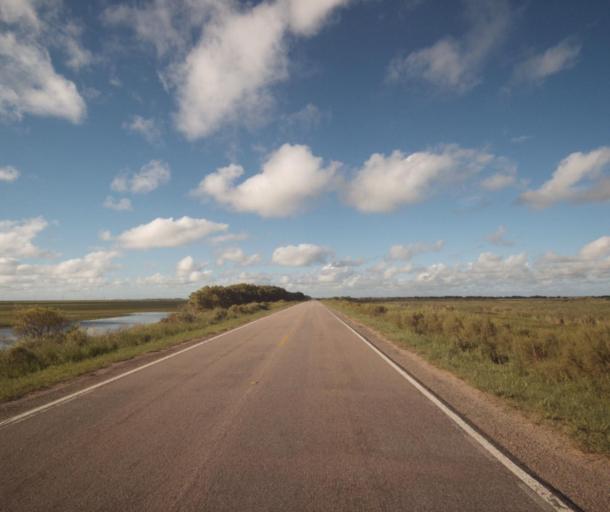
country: BR
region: Rio Grande do Sul
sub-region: Arroio Grande
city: Arroio Grande
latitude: -32.5998
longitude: -52.5691
